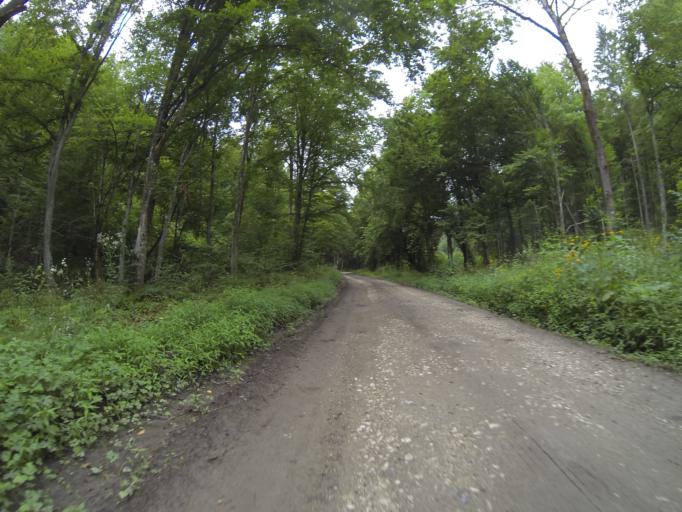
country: RO
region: Brasov
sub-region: Comuna Sinca Veche
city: Sinca Veche
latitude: 45.6953
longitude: 25.1651
